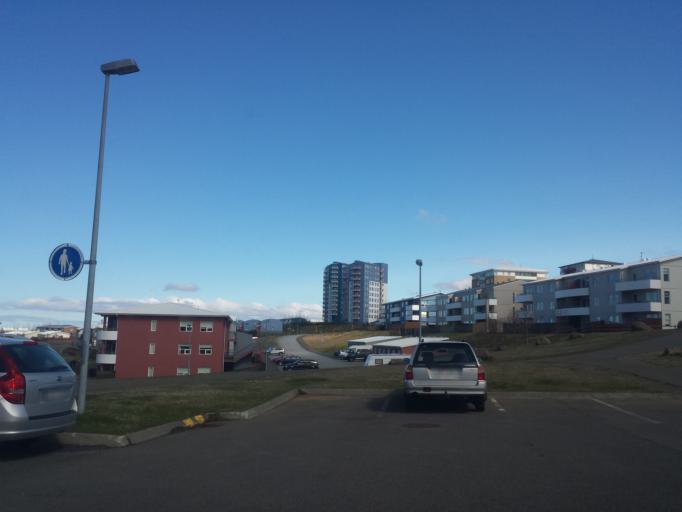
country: IS
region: Capital Region
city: Reykjavik
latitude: 64.0918
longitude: -21.8530
